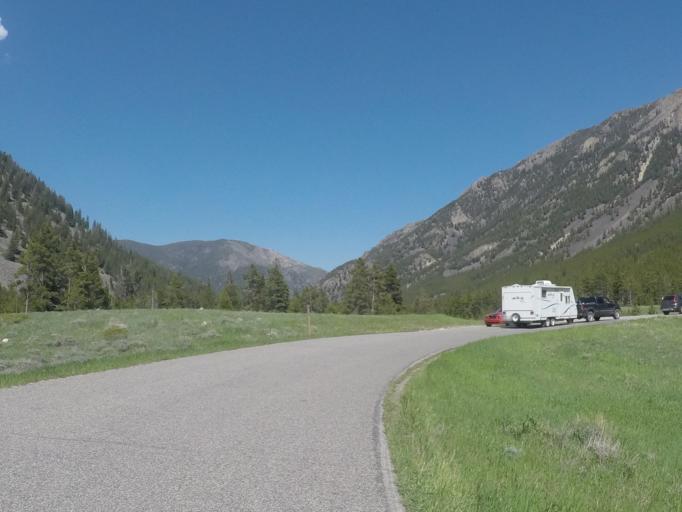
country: US
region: Montana
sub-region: Carbon County
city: Red Lodge
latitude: 45.0646
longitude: -109.3976
